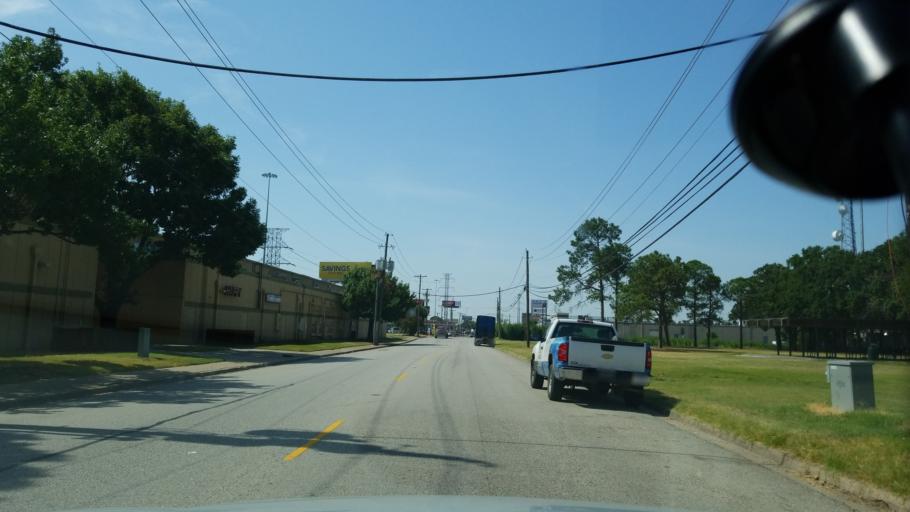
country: US
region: Texas
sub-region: Dallas County
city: Farmers Branch
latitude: 32.8992
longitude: -96.8994
